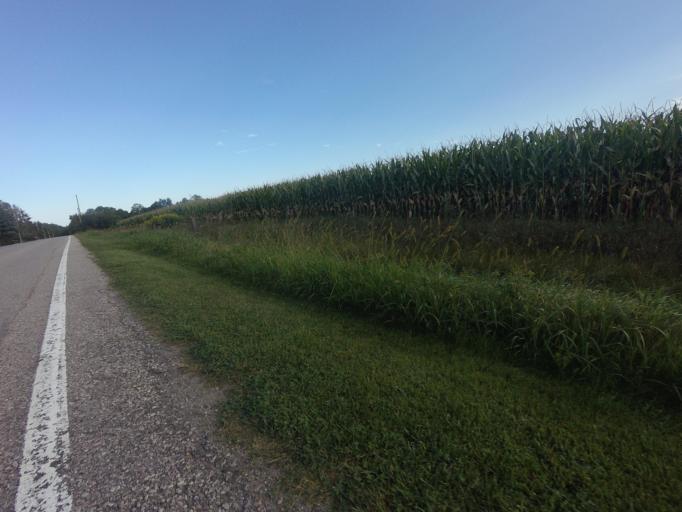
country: CA
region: Ontario
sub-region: Wellington County
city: Guelph
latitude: 43.6009
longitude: -80.3470
